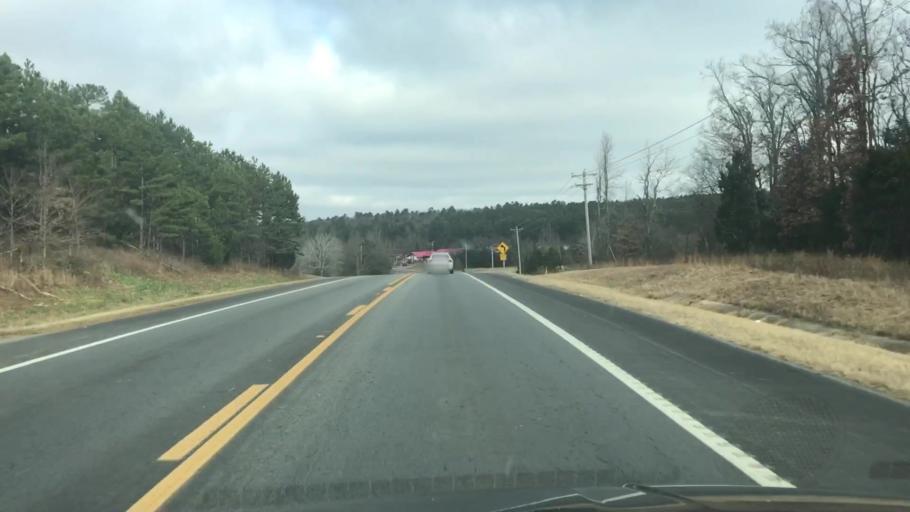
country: US
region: Arkansas
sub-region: Scott County
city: Waldron
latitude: 34.8343
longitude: -94.0437
